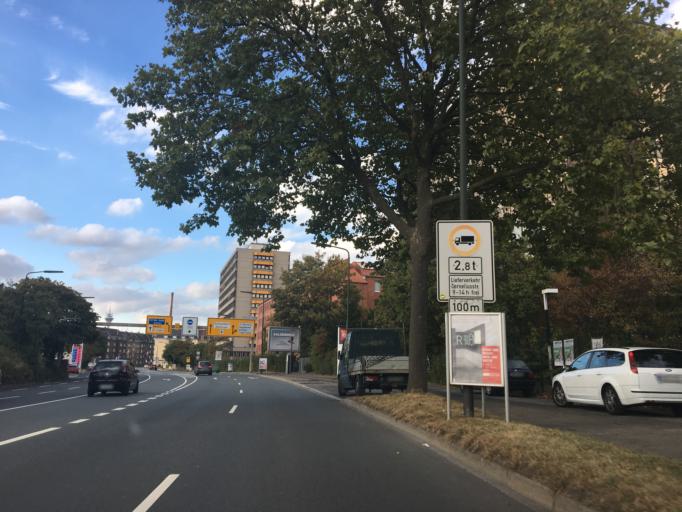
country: DE
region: North Rhine-Westphalia
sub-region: Regierungsbezirk Dusseldorf
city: Dusseldorf
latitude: 51.2019
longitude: 6.7871
